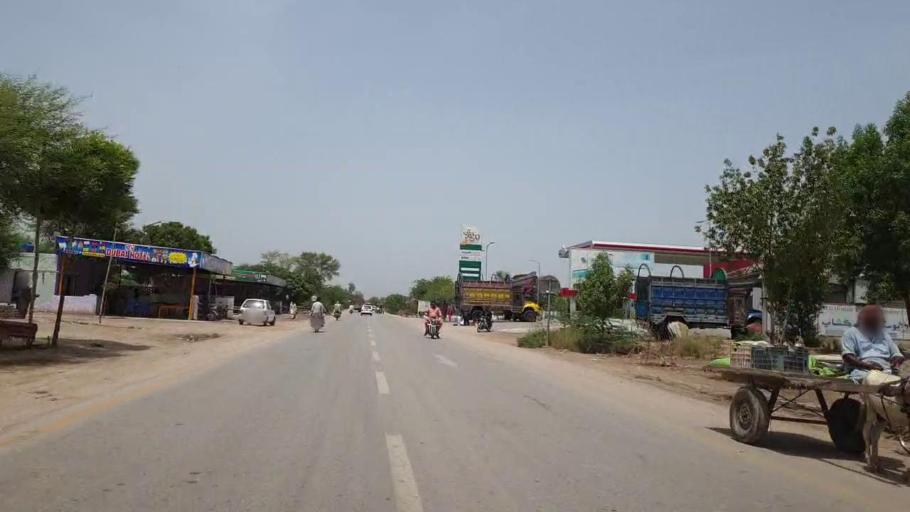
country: PK
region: Sindh
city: Nawabshah
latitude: 26.2454
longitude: 68.4418
